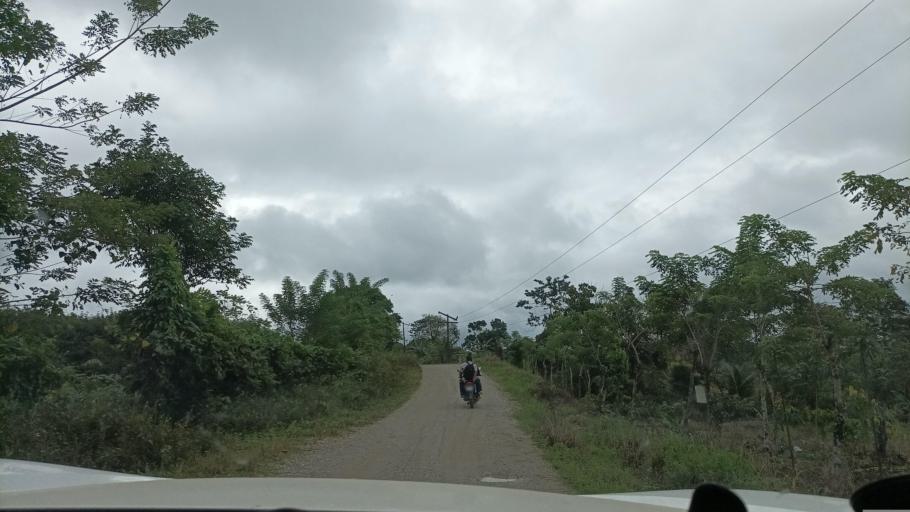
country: MX
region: Veracruz
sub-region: Uxpanapa
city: Poblado 10
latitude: 17.4125
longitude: -94.4171
